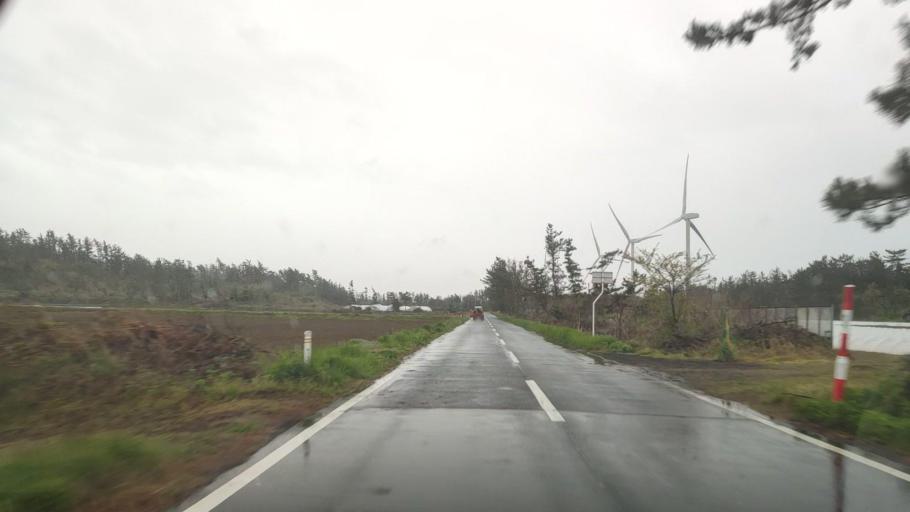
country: JP
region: Akita
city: Noshiromachi
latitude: 40.0726
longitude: 139.9497
